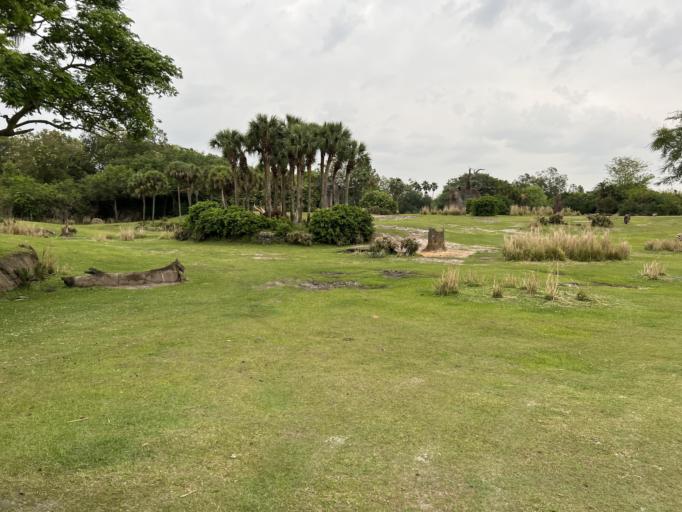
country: US
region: Florida
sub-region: Polk County
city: Citrus Ridge
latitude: 28.3639
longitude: -81.5944
